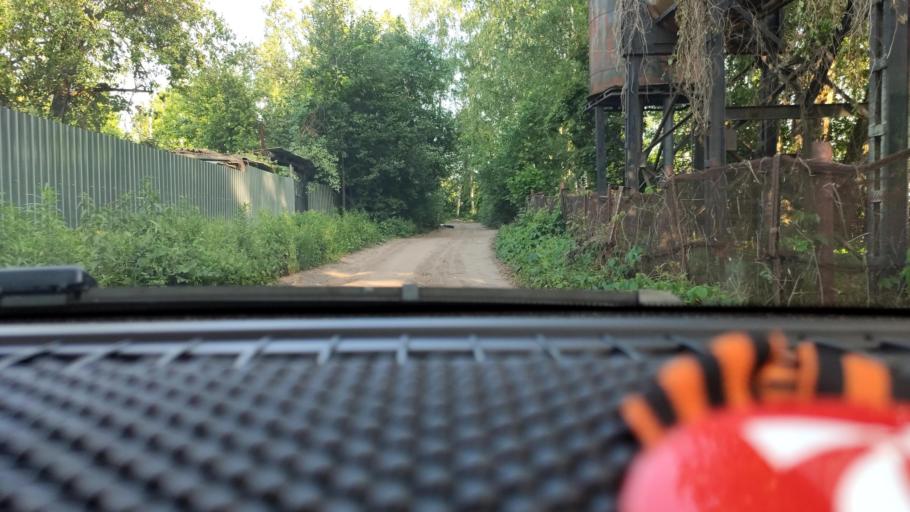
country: RU
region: Voronezj
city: Maslovka
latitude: 51.5926
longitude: 39.1682
